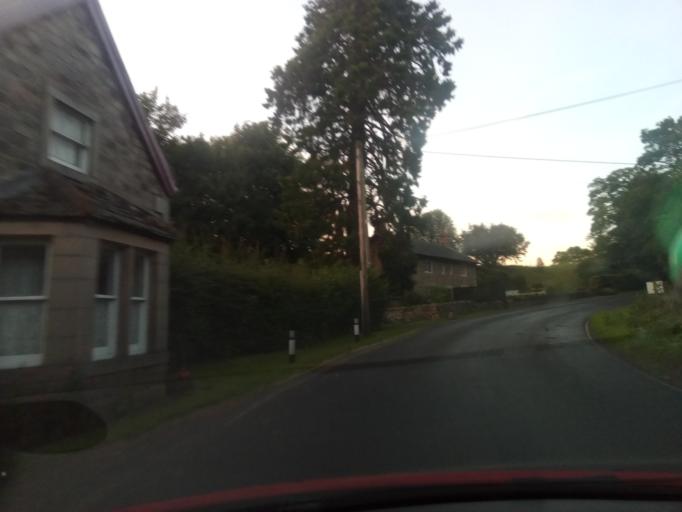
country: GB
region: England
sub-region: Northumberland
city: Bardon Mill
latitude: 54.8930
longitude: -2.3534
